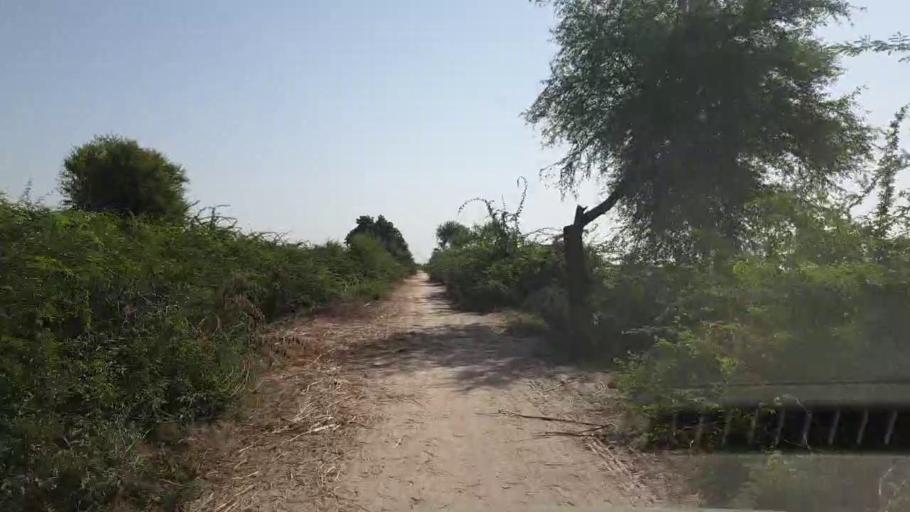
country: PK
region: Sindh
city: Kadhan
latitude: 24.6213
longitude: 68.9959
